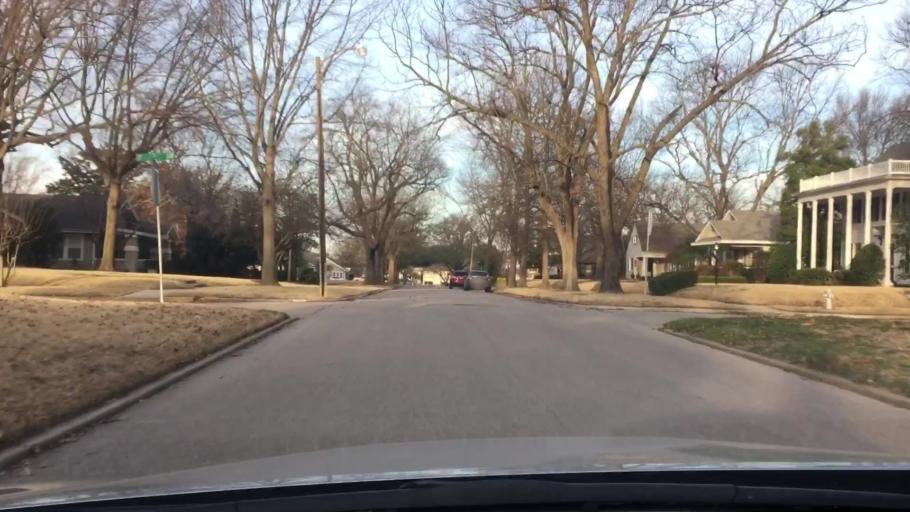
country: US
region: Oklahoma
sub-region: Carter County
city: Ardmore
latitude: 34.1720
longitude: -97.1481
